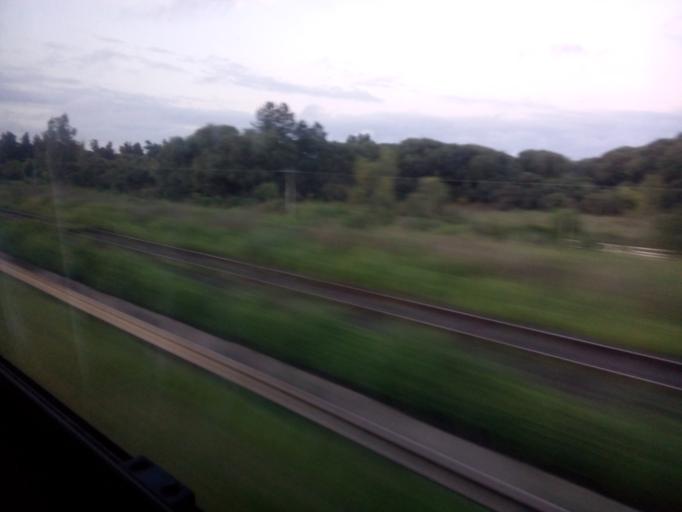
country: AR
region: Buenos Aires
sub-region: Partido de Zarate
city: Zarate
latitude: -34.0601
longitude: -58.9903
